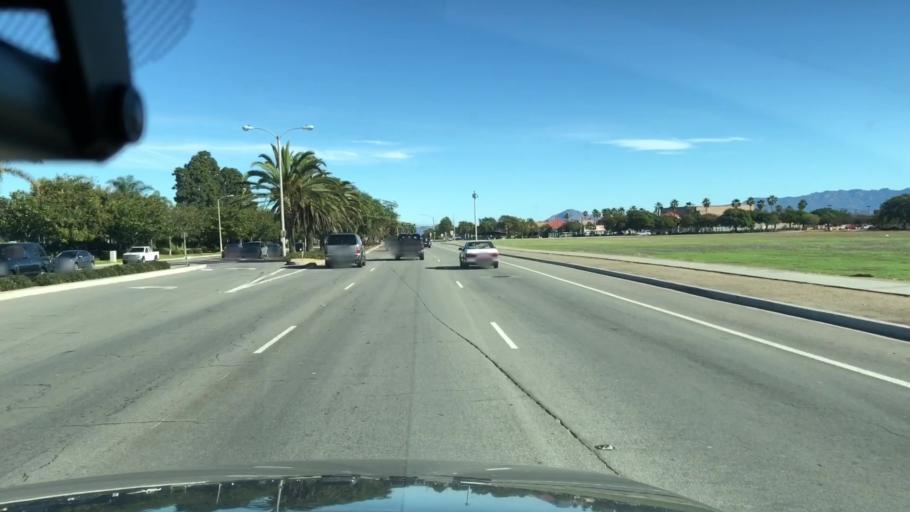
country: US
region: California
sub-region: Ventura County
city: El Rio
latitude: 34.2190
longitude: -119.1756
